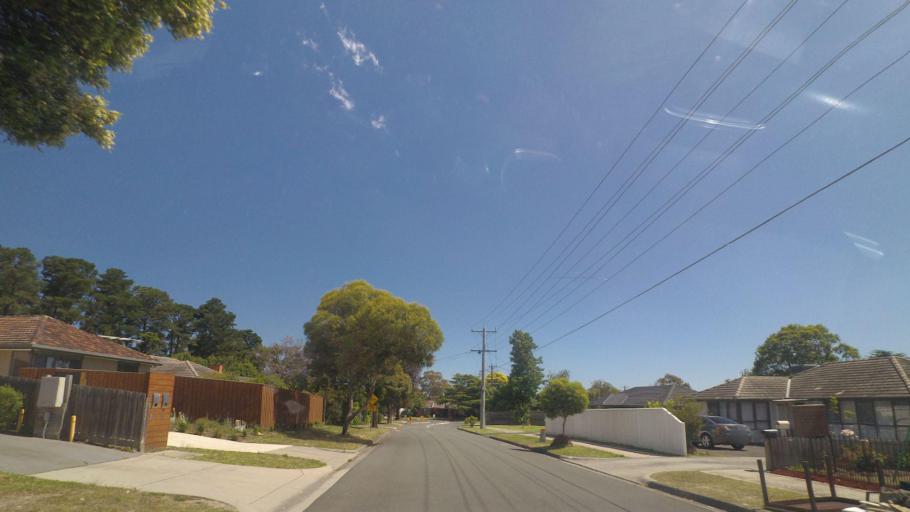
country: AU
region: Victoria
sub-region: Yarra Ranges
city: Kilsyth
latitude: -37.8081
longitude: 145.3248
